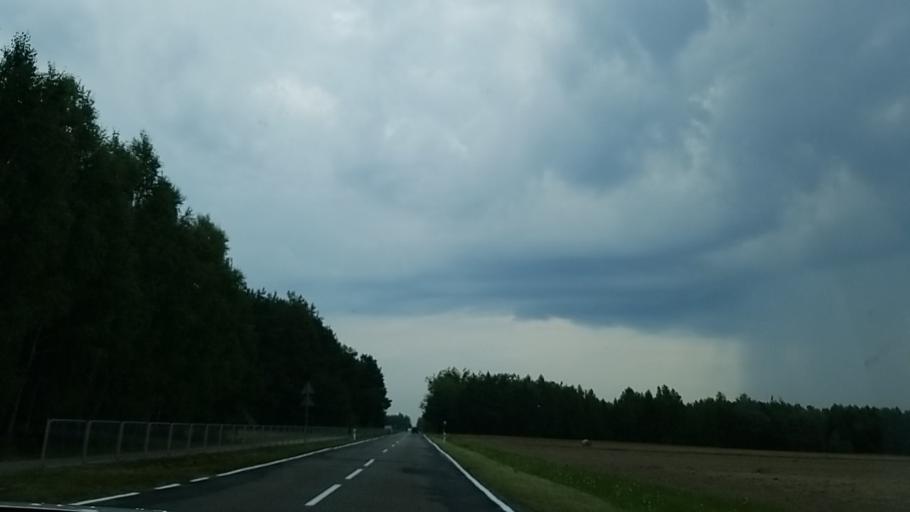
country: PL
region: Lublin Voivodeship
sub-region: Powiat bialski
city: Slawatycze
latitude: 51.7310
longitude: 23.5174
